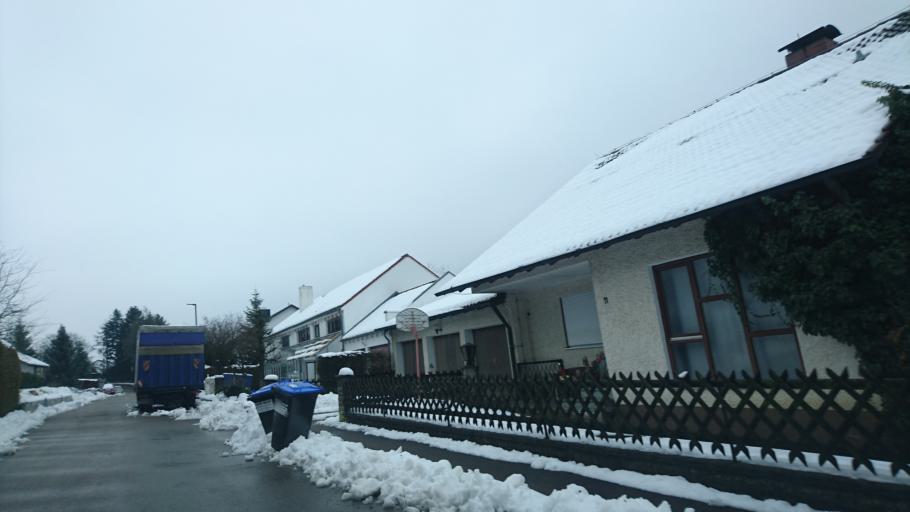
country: DE
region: Bavaria
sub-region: Swabia
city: Landensberg
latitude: 48.4346
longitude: 10.5117
